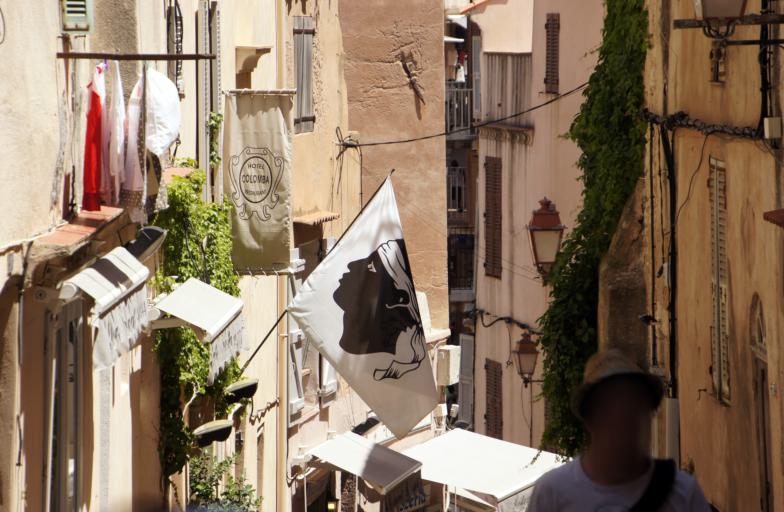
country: FR
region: Corsica
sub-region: Departement de la Corse-du-Sud
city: Bonifacio
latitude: 41.3864
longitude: 9.1566
